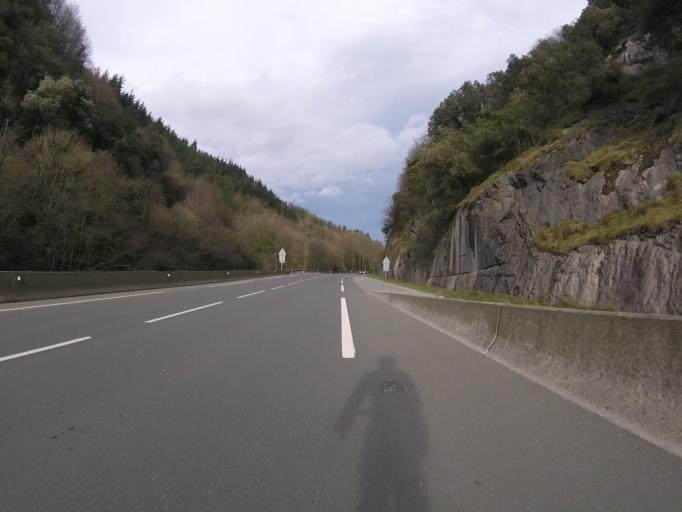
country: ES
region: Basque Country
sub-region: Provincia de Guipuzcoa
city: Cestona
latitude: 43.2477
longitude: -2.2602
